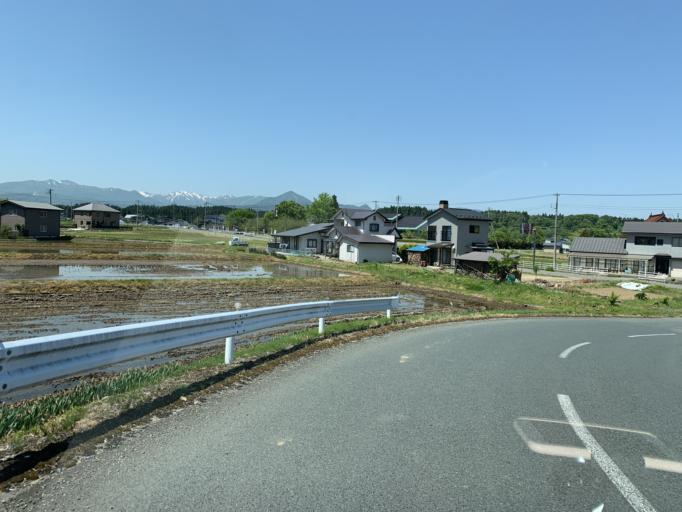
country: JP
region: Iwate
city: Kitakami
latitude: 39.2759
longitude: 141.0487
